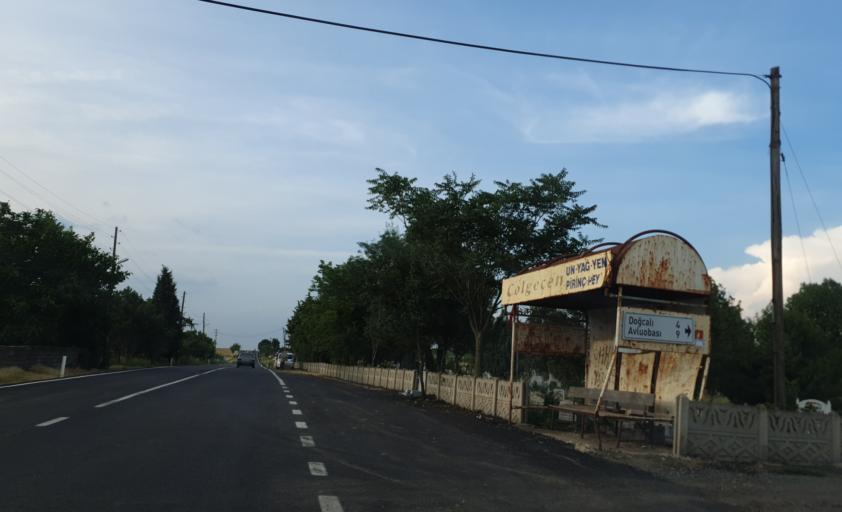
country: TR
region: Tekirdag
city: Hayrabolu
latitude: 41.2924
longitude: 27.1344
